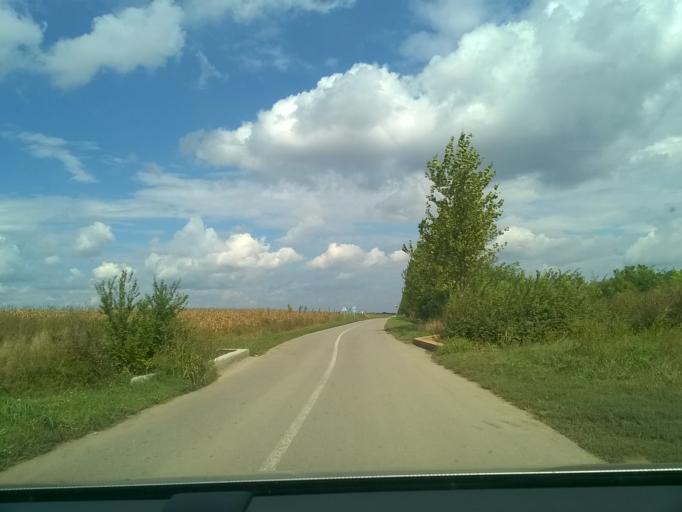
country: RS
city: Debeljaca
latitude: 45.0829
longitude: 20.6026
